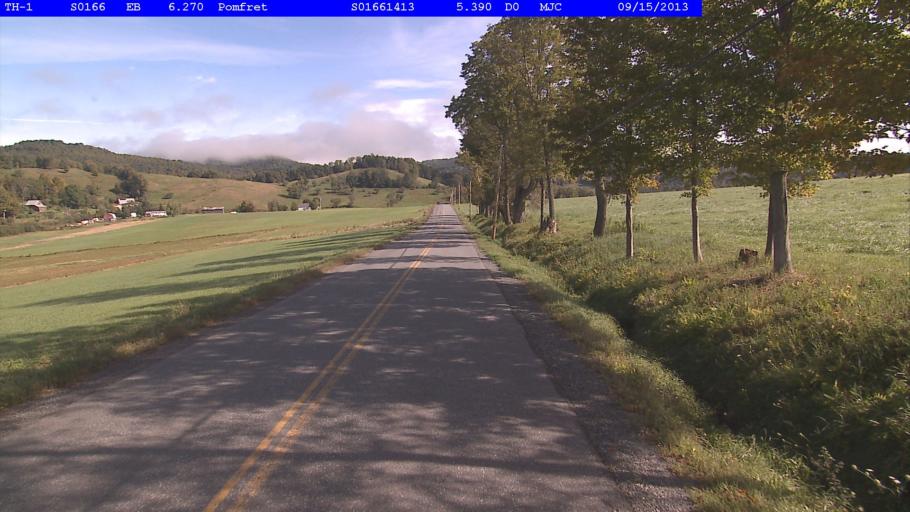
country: US
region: Vermont
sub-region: Windsor County
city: Woodstock
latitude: 43.7179
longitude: -72.5043
